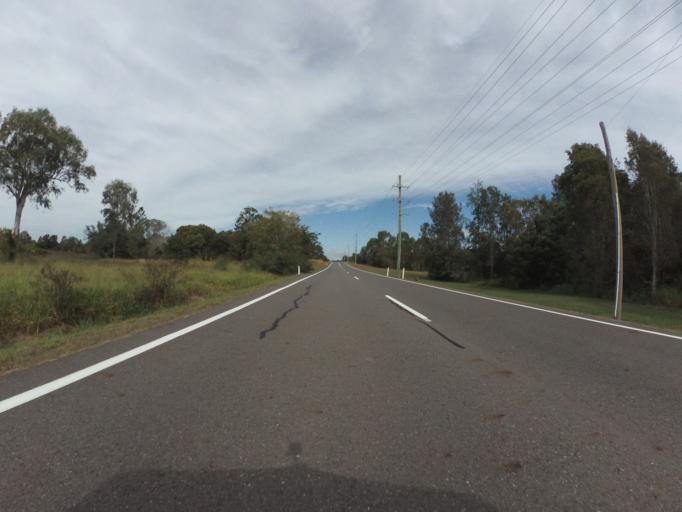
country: AU
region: Queensland
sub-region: Brisbane
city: Moggill
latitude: -27.5868
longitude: 152.8611
